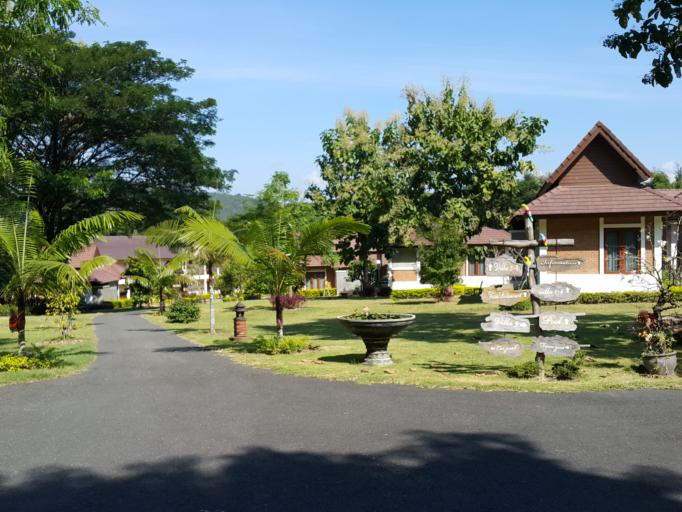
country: TH
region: Chiang Mai
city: Mae On
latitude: 18.8261
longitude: 99.1866
